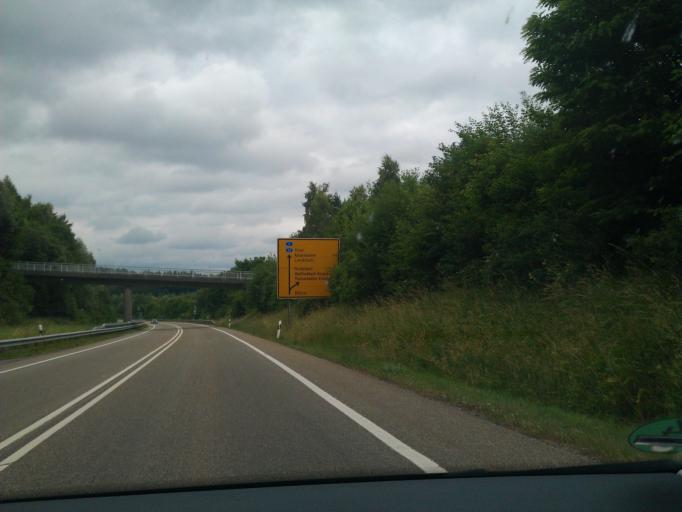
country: DE
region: Rheinland-Pfalz
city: Thaleischweiler-Froschen
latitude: 49.2507
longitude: 7.5875
